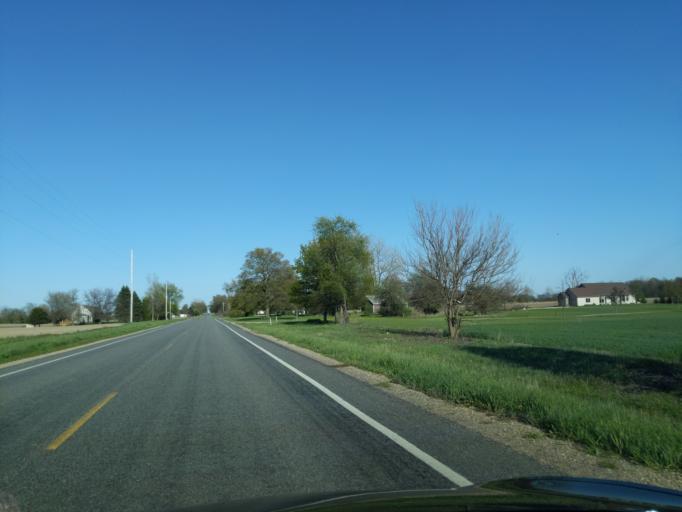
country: US
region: Michigan
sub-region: Ionia County
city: Ionia
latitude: 42.8861
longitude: -85.0974
